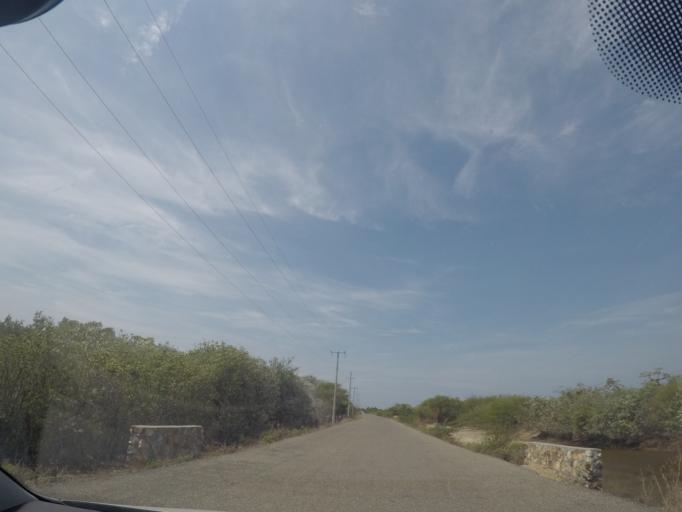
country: MX
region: Oaxaca
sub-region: Salina Cruz
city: Salina Cruz
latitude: 16.1972
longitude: -95.1195
